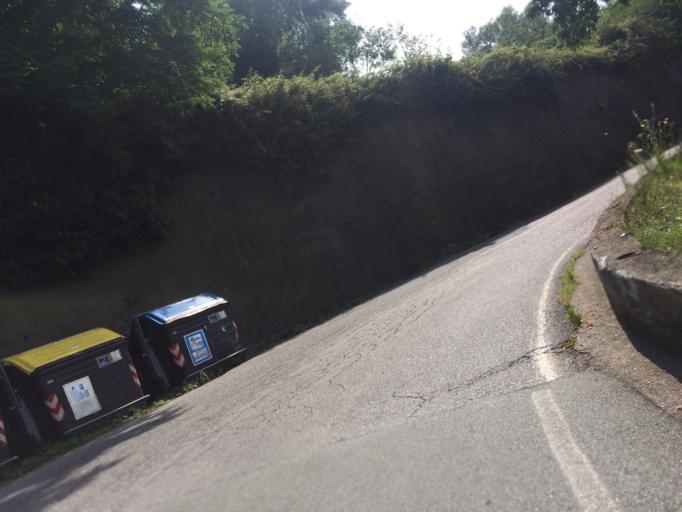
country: IT
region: Liguria
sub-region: Provincia di Savona
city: Varazze
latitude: 44.3793
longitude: 8.5700
